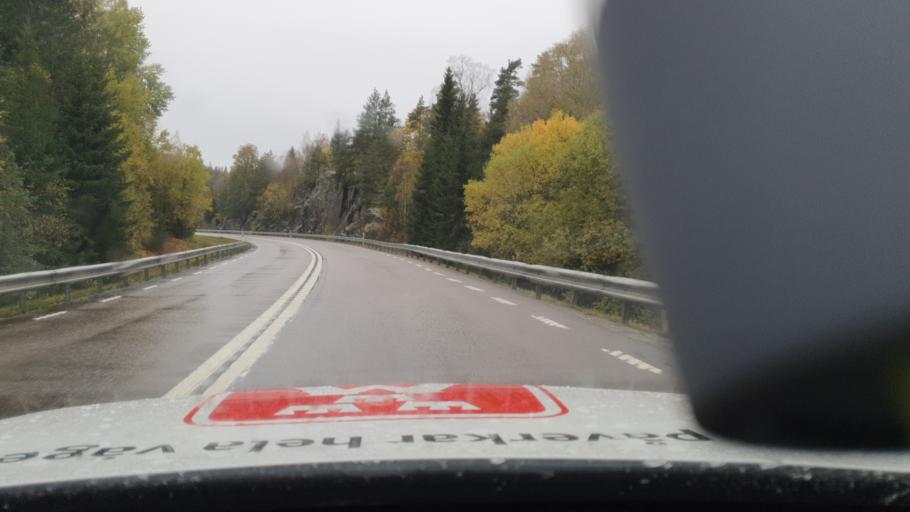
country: SE
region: Vaestra Goetaland
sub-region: Dals-Ed Kommun
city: Ed
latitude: 58.9349
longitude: 12.0508
